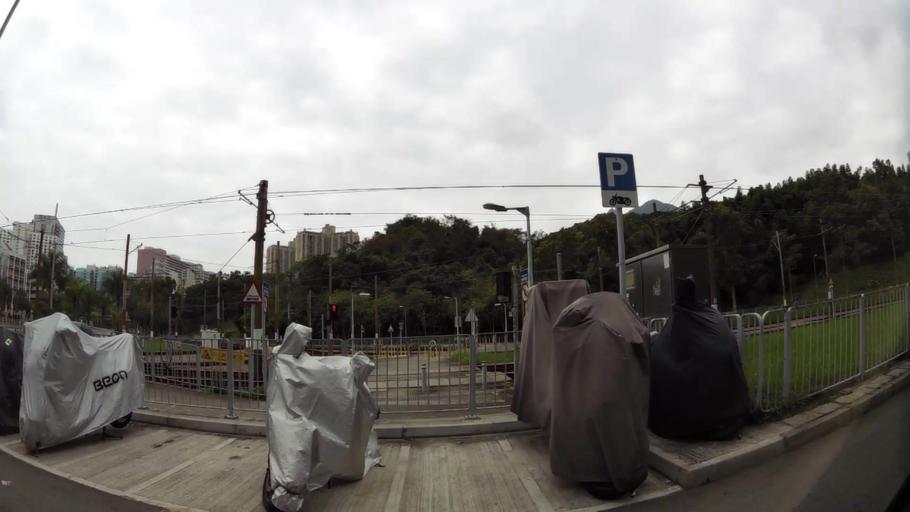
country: HK
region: Tuen Mun
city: Tuen Mun
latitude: 22.4047
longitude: 113.9665
